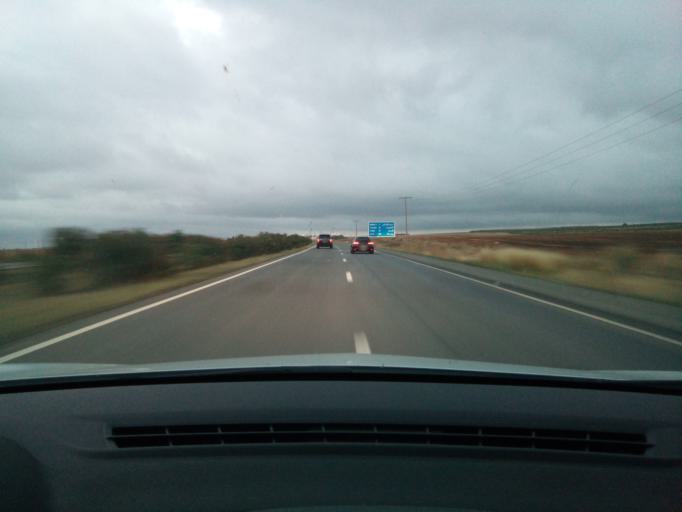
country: MA
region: Meknes-Tafilalet
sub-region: Meknes
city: Meknes
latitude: 33.8343
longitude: -5.5832
